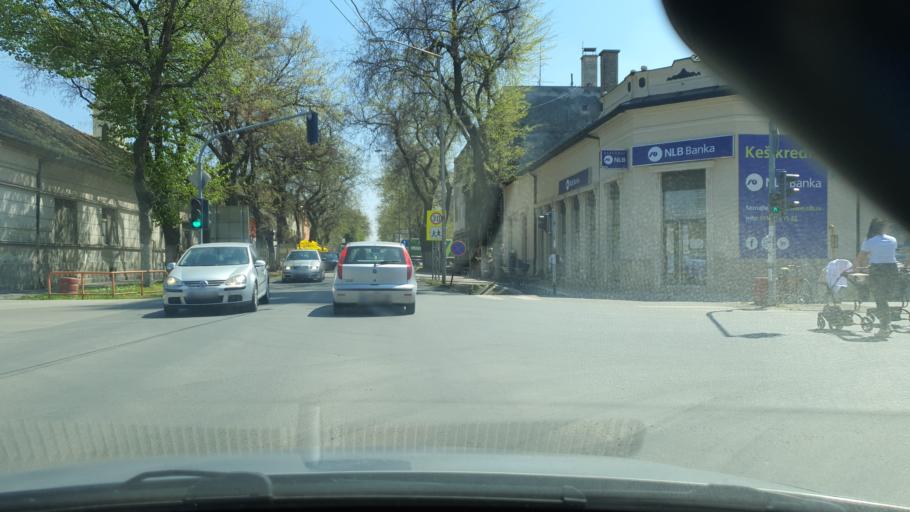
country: RS
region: Autonomna Pokrajina Vojvodina
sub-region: Zapadnobacki Okrug
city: Odzaci
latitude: 45.5072
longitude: 19.2581
